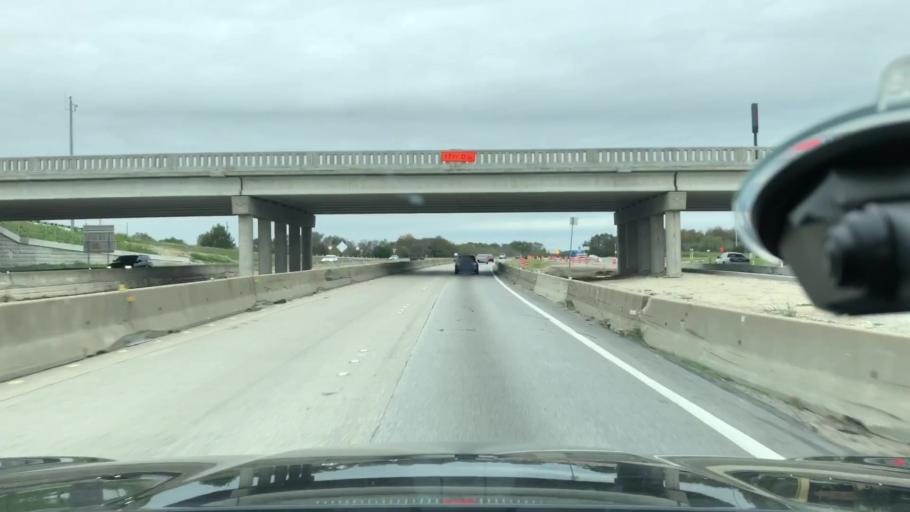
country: US
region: Texas
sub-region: Ellis County
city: Waxahachie
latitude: 32.3995
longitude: -96.8722
